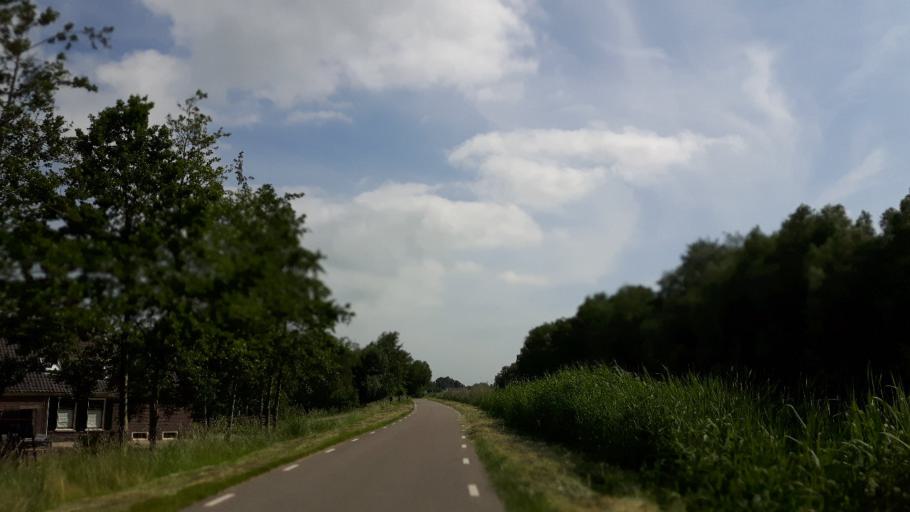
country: NL
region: Utrecht
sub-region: Gemeente De Ronde Venen
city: Mijdrecht
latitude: 52.1695
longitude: 4.8686
